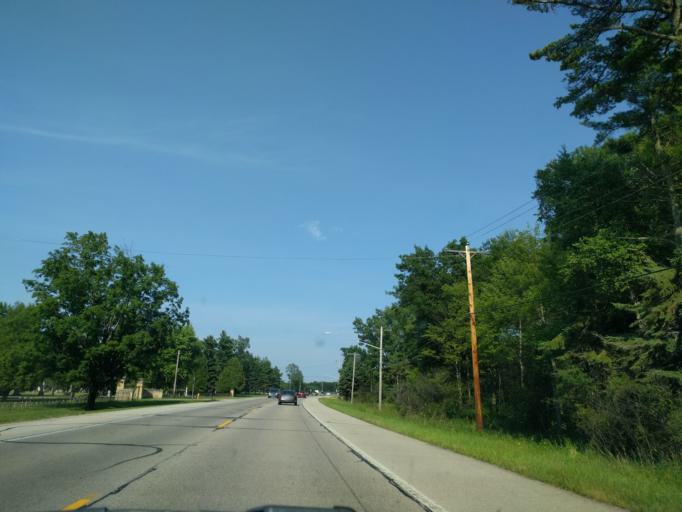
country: US
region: Michigan
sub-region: Delta County
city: Escanaba
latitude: 45.7120
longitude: -87.0922
